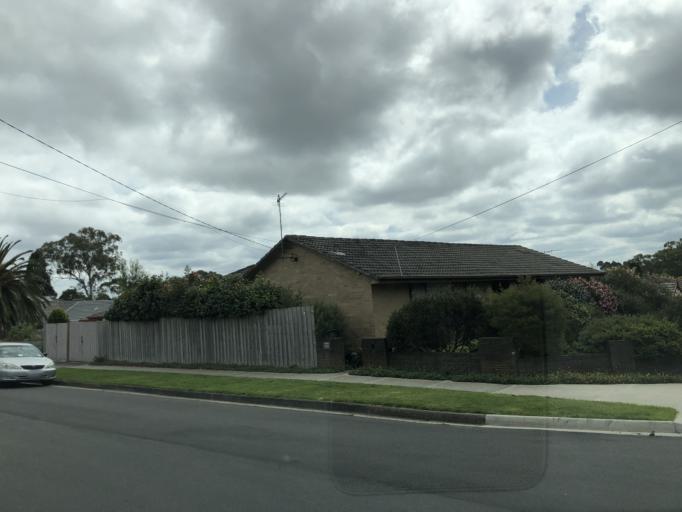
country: AU
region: Victoria
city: Burwood East
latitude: -37.8450
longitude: 145.1485
